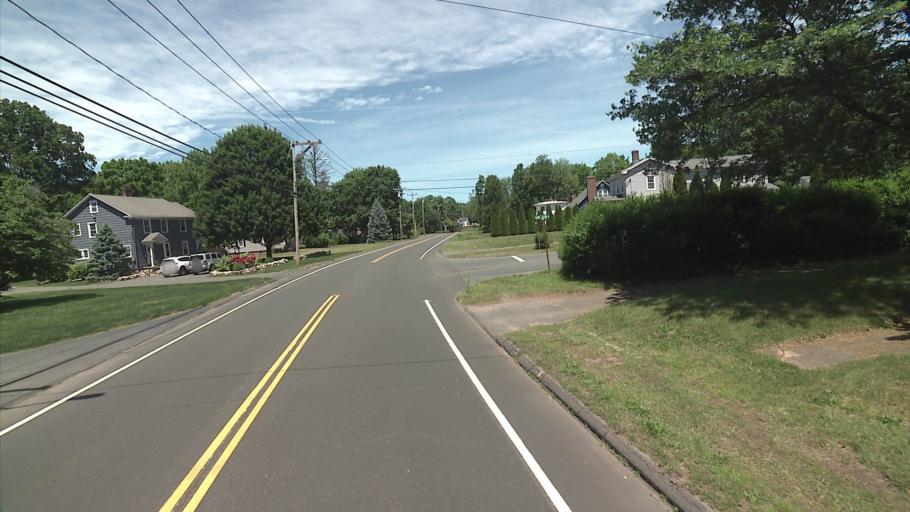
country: US
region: Connecticut
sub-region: New Haven County
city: Meriden
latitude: 41.5893
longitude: -72.8740
